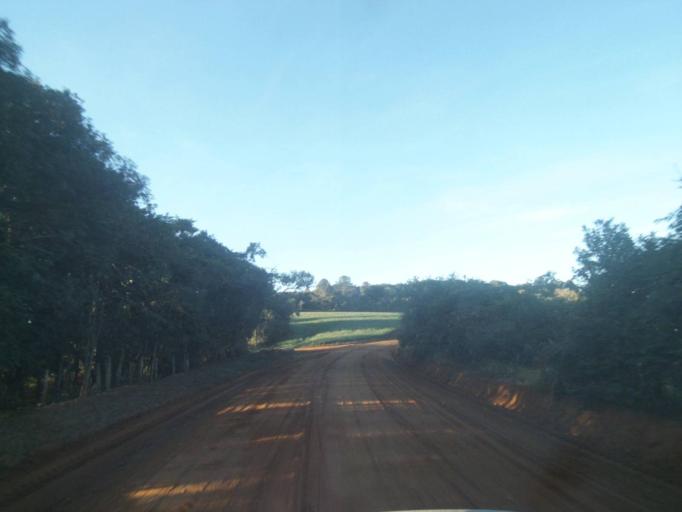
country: BR
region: Parana
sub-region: Tibagi
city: Tibagi
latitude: -24.5470
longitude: -50.5636
